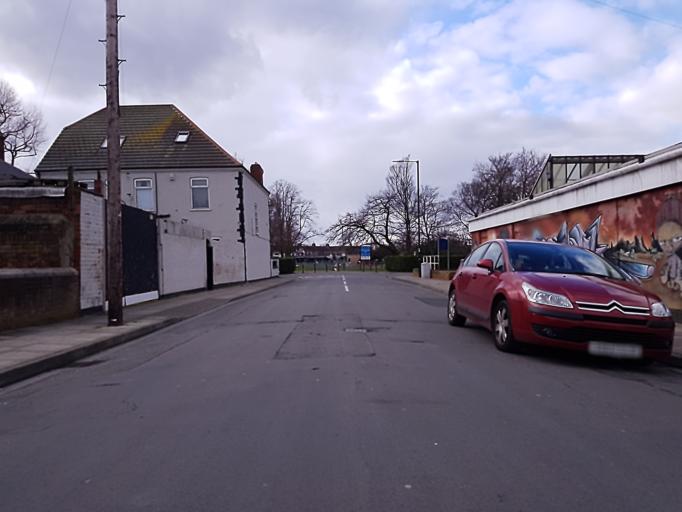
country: GB
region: England
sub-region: North East Lincolnshire
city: Grimsby
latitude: 53.5665
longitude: -0.0627
